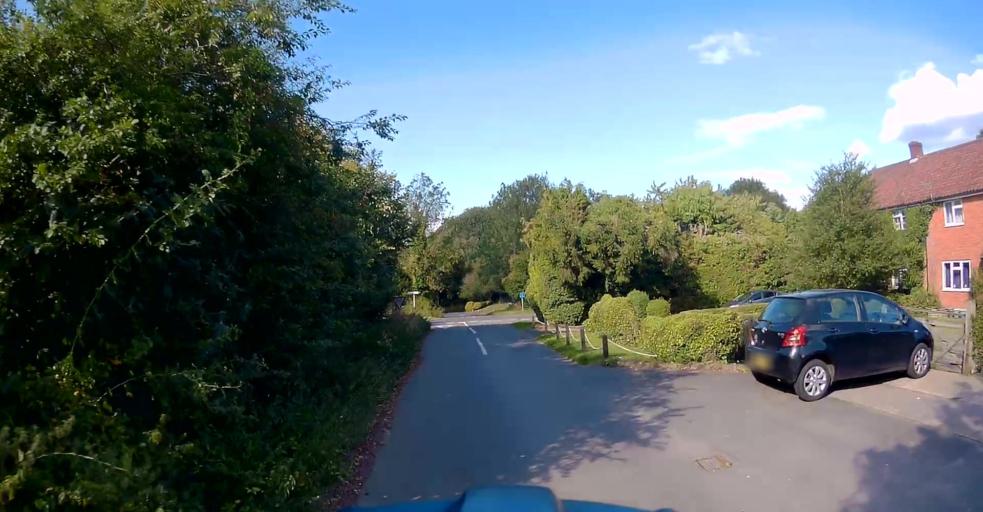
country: GB
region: England
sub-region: Hampshire
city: Old Basing
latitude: 51.2630
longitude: -1.0219
